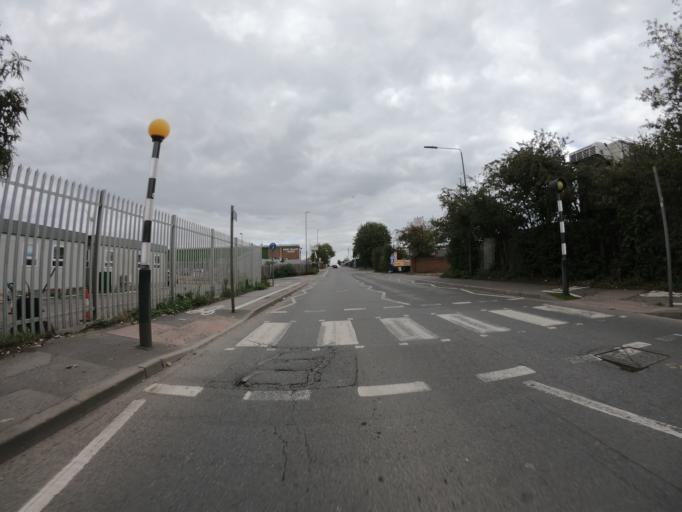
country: GB
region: England
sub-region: Greater London
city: Erith
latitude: 51.4776
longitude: 0.1919
